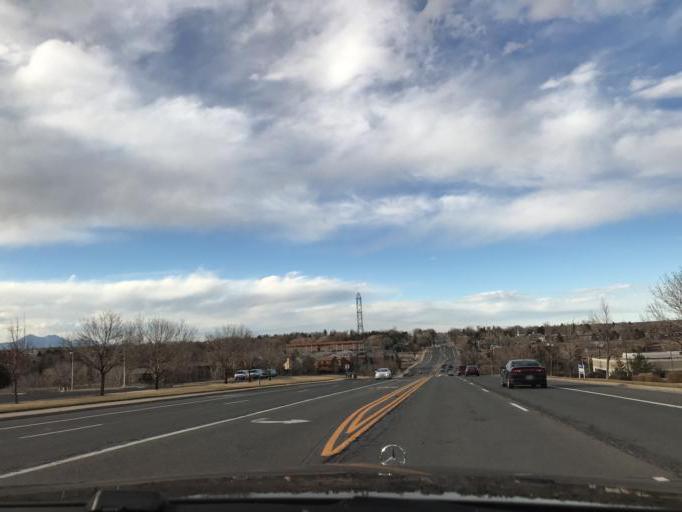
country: US
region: Colorado
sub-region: Jefferson County
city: Applewood
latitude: 39.7957
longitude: -105.1380
